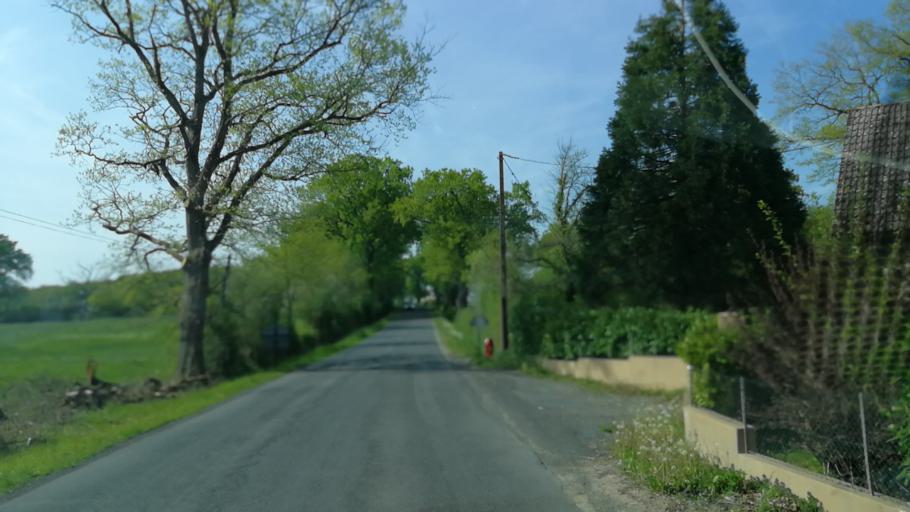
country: FR
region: Auvergne
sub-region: Departement de l'Allier
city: Neuilly-le-Real
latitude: 46.4897
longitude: 3.5195
